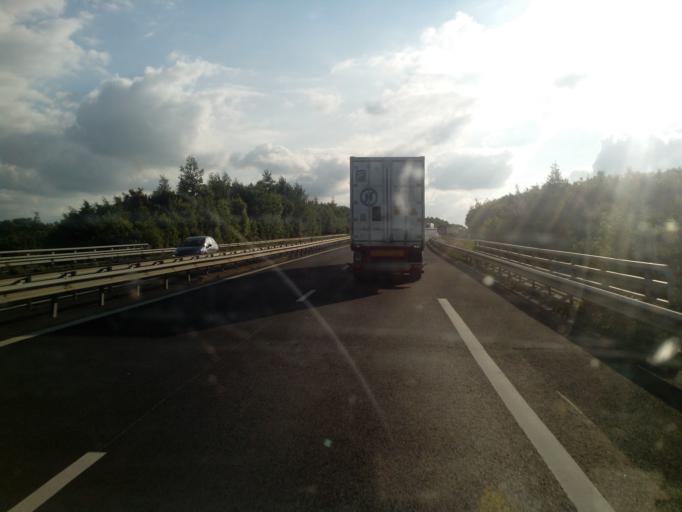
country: FR
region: Lower Normandy
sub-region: Departement du Calvados
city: Cahagnes
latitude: 49.0509
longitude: -0.7127
